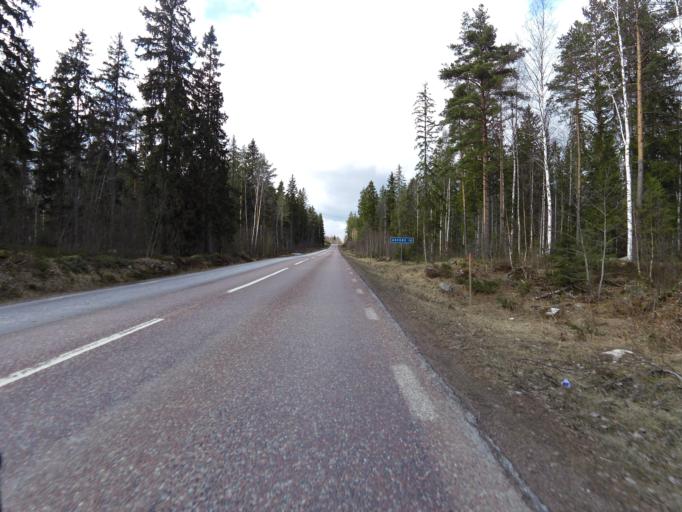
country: SE
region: Gaevleborg
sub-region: Hofors Kommun
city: Hofors
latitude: 60.5010
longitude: 16.4292
